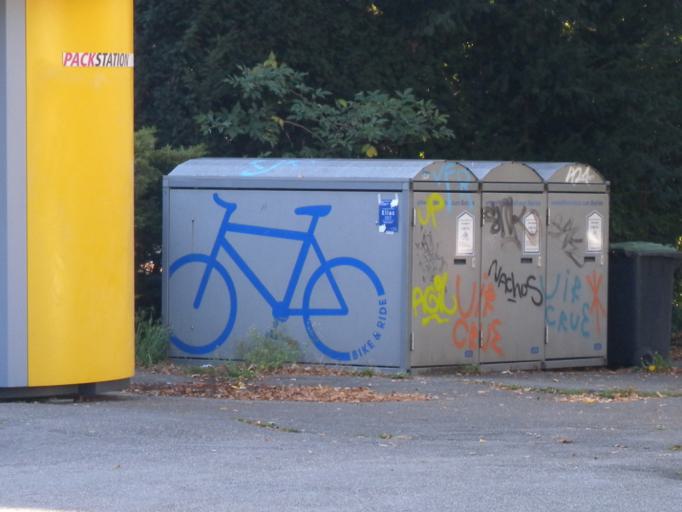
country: DE
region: Baden-Wuerttemberg
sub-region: Freiburg Region
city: Freiburg
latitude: 47.9827
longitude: 7.8548
